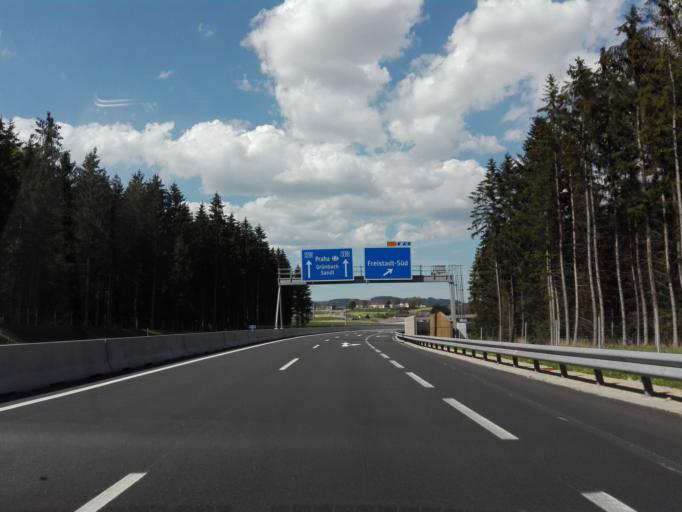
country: AT
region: Upper Austria
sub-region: Politischer Bezirk Freistadt
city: Freistadt
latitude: 48.4789
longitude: 14.5007
